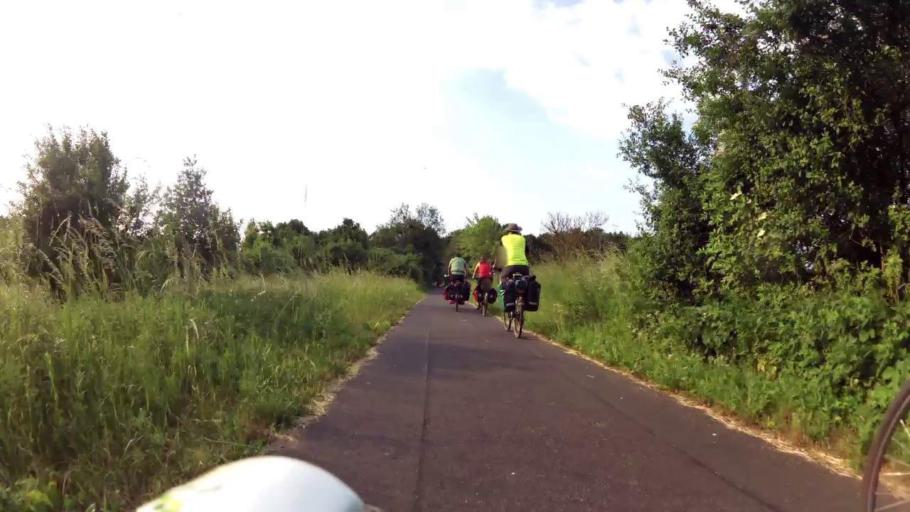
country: PL
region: Kujawsko-Pomorskie
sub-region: Powiat torunski
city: Lubianka
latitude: 53.1416
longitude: 18.4595
